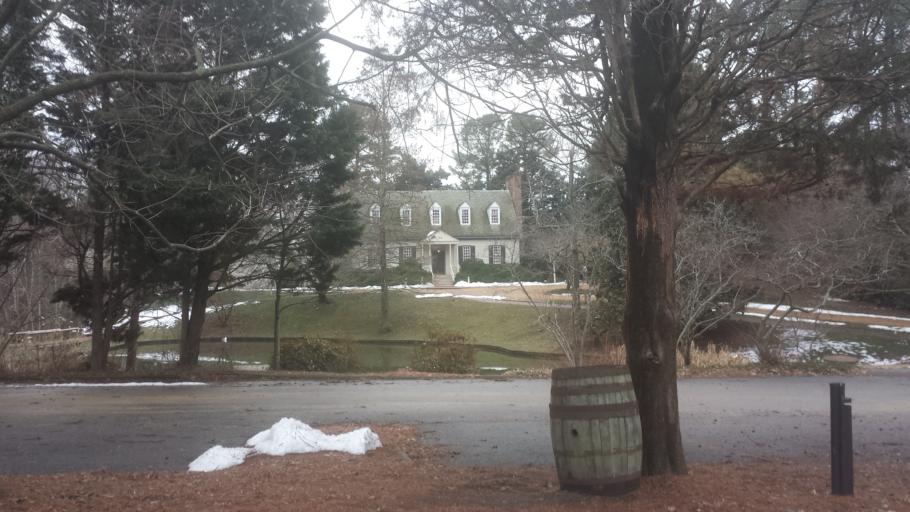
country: US
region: Virginia
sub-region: City of Williamsburg
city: Williamsburg
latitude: 37.2688
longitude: -76.6968
